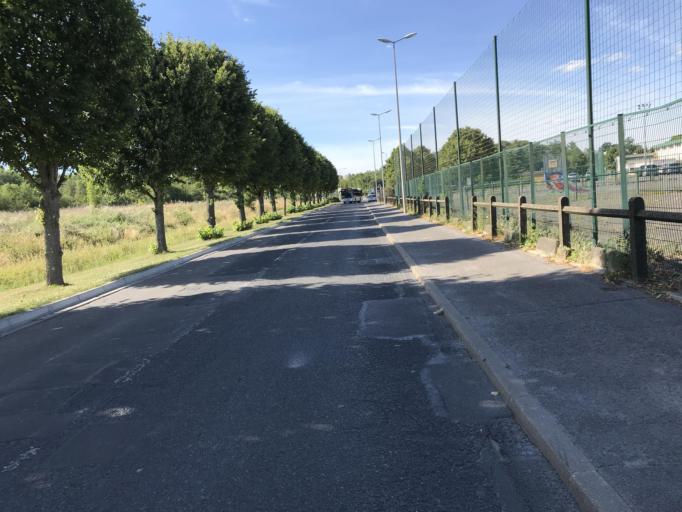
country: FR
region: Ile-de-France
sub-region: Departement de l'Essonne
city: Fleury-Merogis
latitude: 48.6330
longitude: 2.3606
